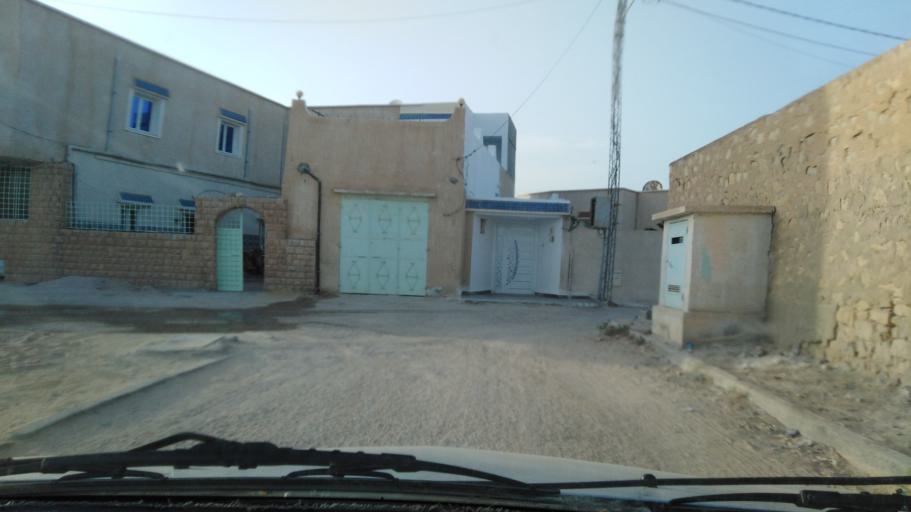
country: TN
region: Qabis
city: Gabes
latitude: 33.9556
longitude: 9.9961
